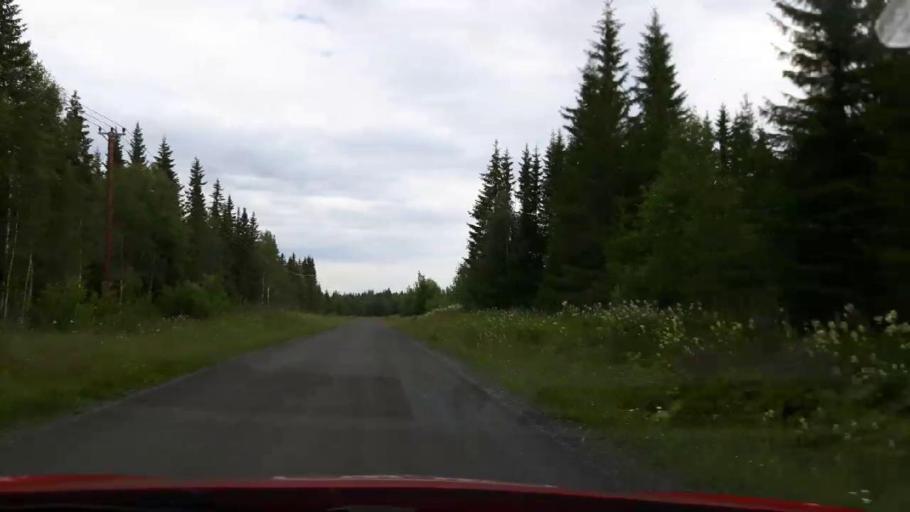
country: SE
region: Jaemtland
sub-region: Stroemsunds Kommun
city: Stroemsund
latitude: 63.4922
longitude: 15.3134
